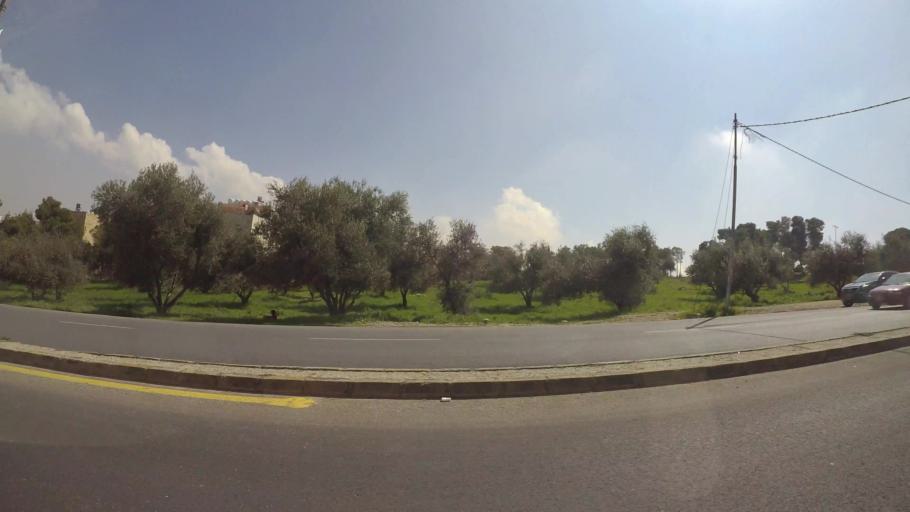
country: JO
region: Amman
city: Al Bunayyat ash Shamaliyah
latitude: 31.9211
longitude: 35.8953
